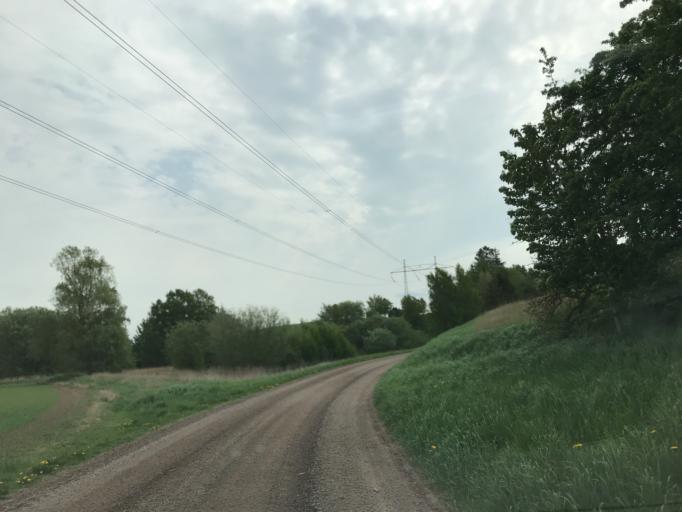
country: SE
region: Skane
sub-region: Svalovs Kommun
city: Teckomatorp
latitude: 55.8330
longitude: 13.0729
